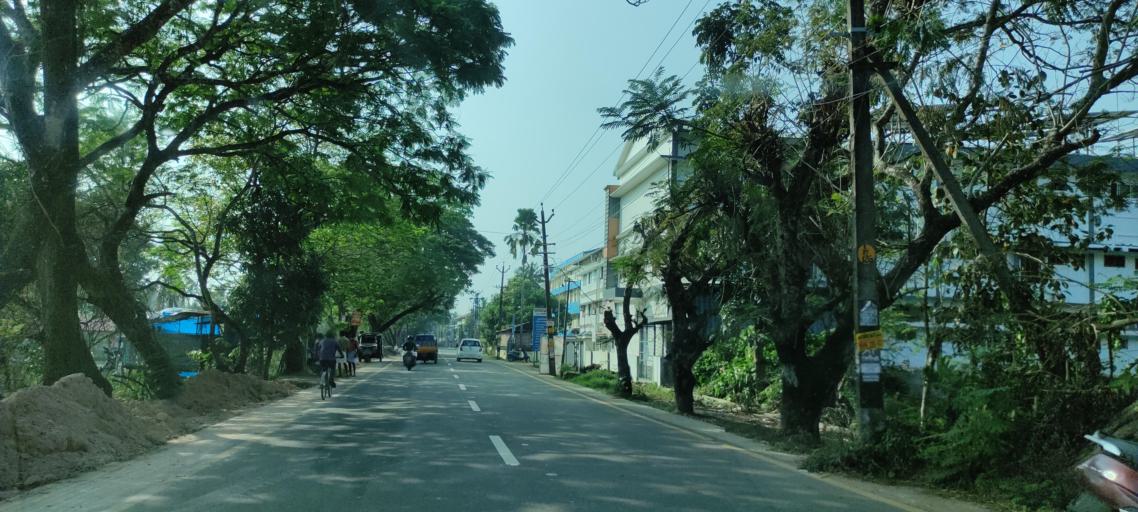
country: IN
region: Kerala
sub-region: Kottayam
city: Changanacheri
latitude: 9.3625
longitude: 76.4536
